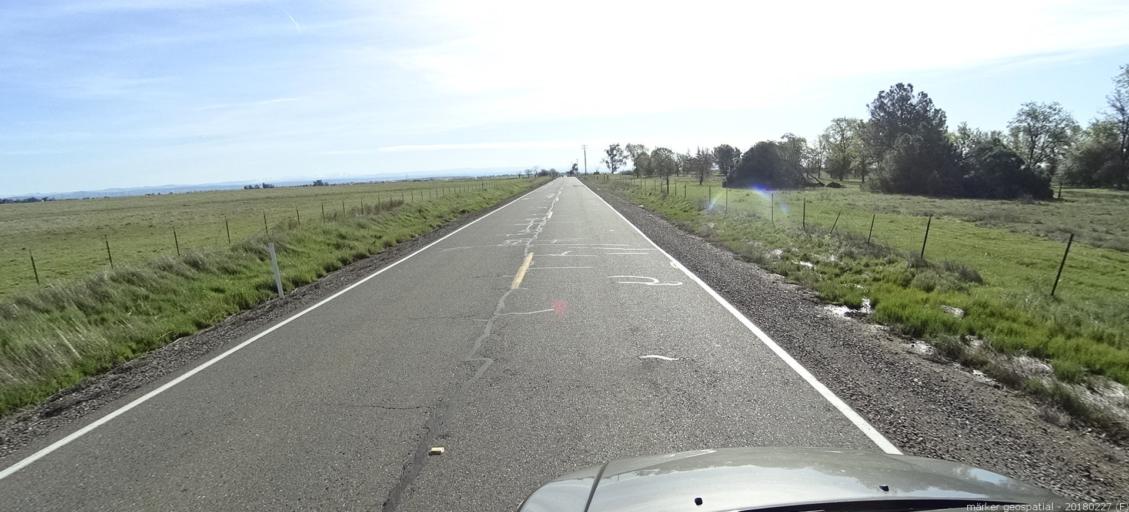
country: US
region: California
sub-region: Sacramento County
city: Vineyard
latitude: 38.4962
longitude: -121.2825
